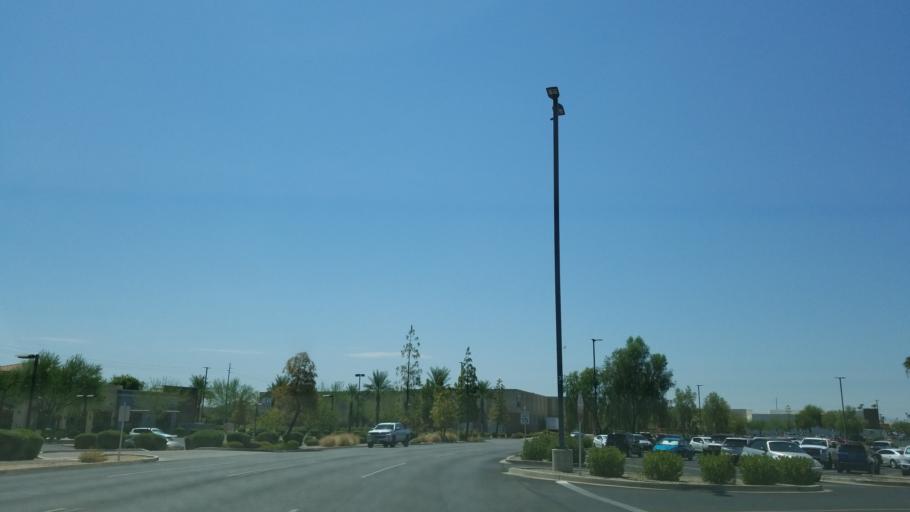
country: US
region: Arizona
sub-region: Maricopa County
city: Peoria
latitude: 33.6414
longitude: -112.2217
